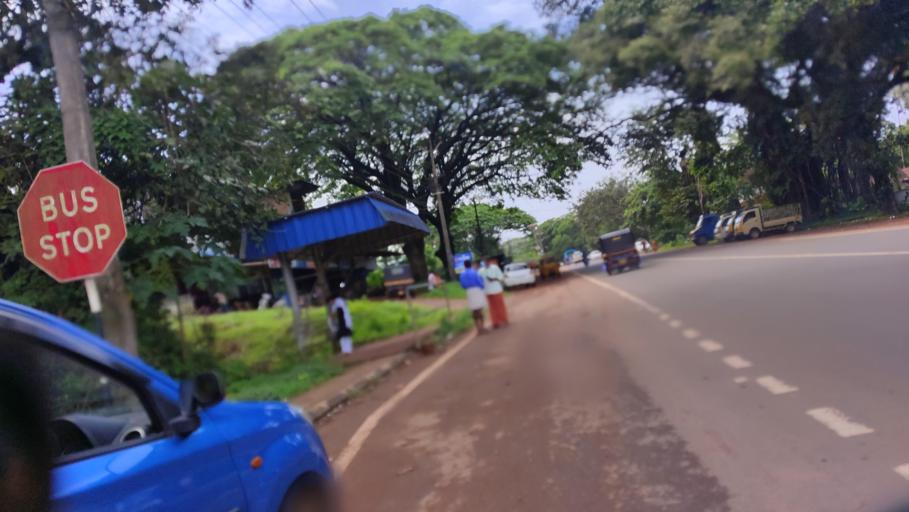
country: IN
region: Kerala
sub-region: Kasaragod District
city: Kannangad
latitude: 12.3900
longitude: 75.0423
